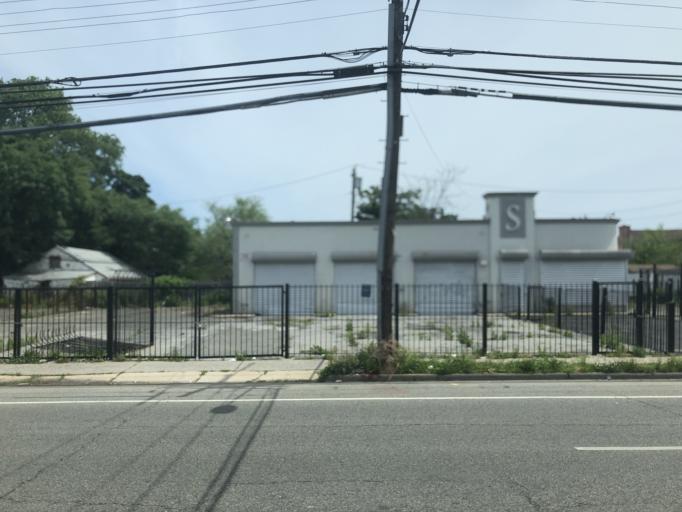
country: US
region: New York
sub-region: Nassau County
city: Hempstead
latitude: 40.7013
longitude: -73.6243
